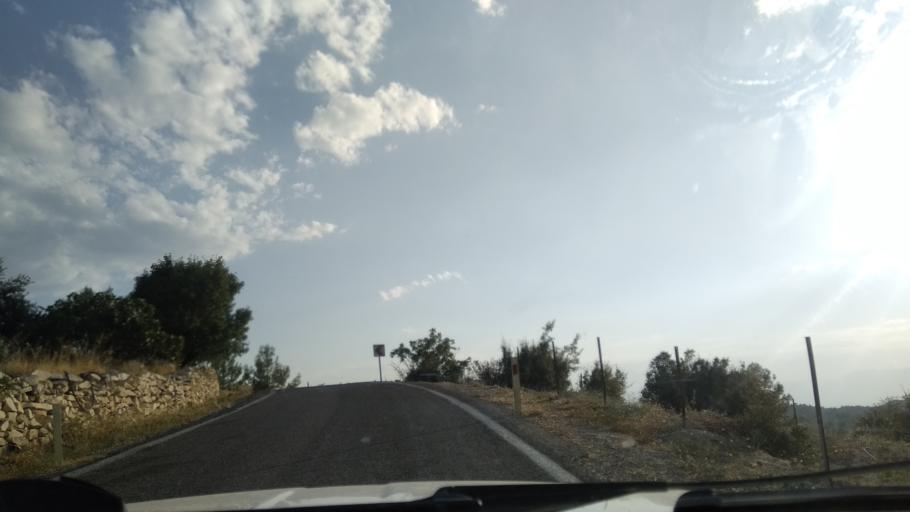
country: TR
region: Mersin
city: Sarikavak
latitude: 36.5752
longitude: 33.6396
